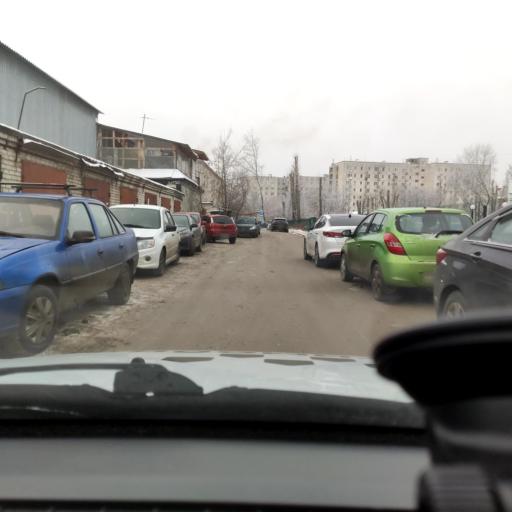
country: RU
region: Perm
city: Perm
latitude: 57.9722
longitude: 56.2420
